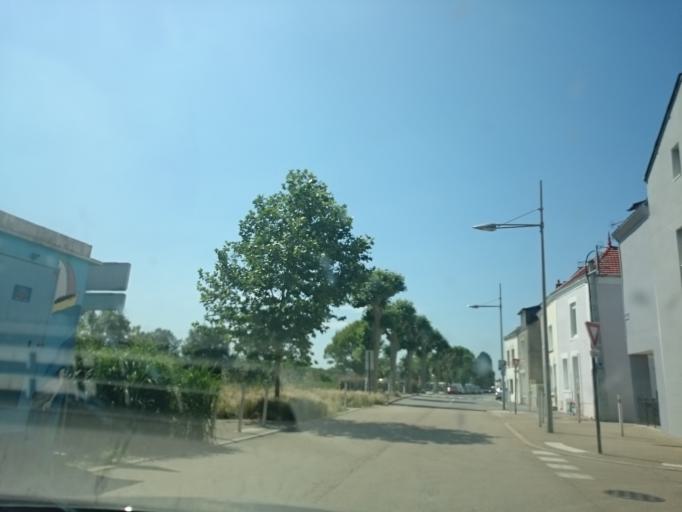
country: FR
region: Pays de la Loire
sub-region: Departement de la Loire-Atlantique
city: Indre
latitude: 47.1994
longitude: -1.6758
